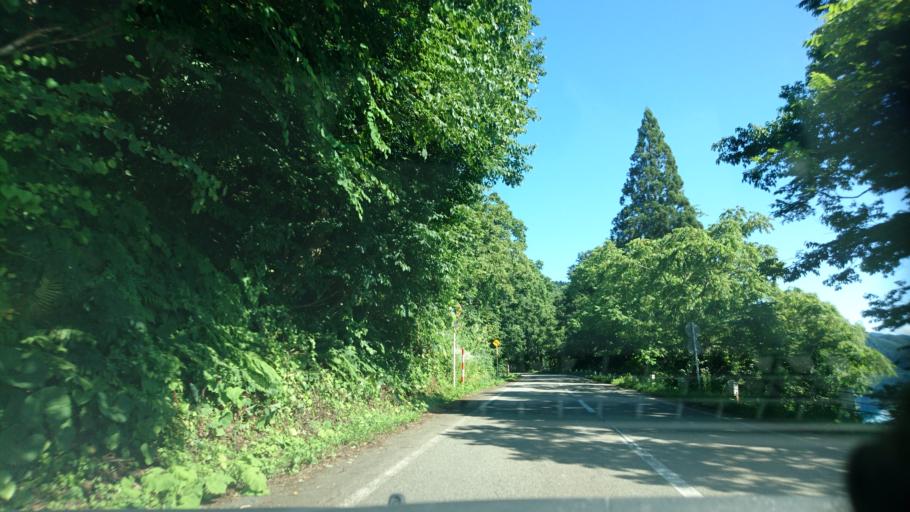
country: JP
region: Akita
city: Kakunodatemachi
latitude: 39.7169
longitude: 140.6304
